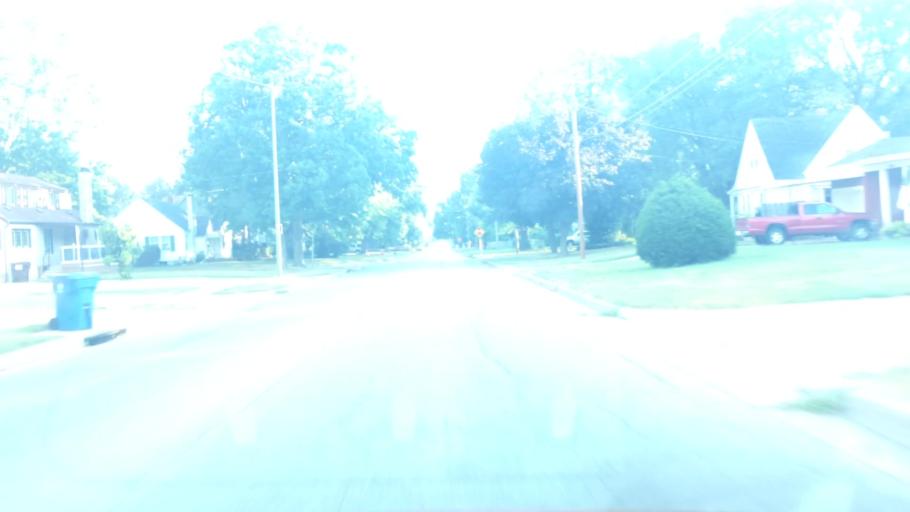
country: US
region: Missouri
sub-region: Greene County
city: Springfield
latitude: 37.1835
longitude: -93.2715
